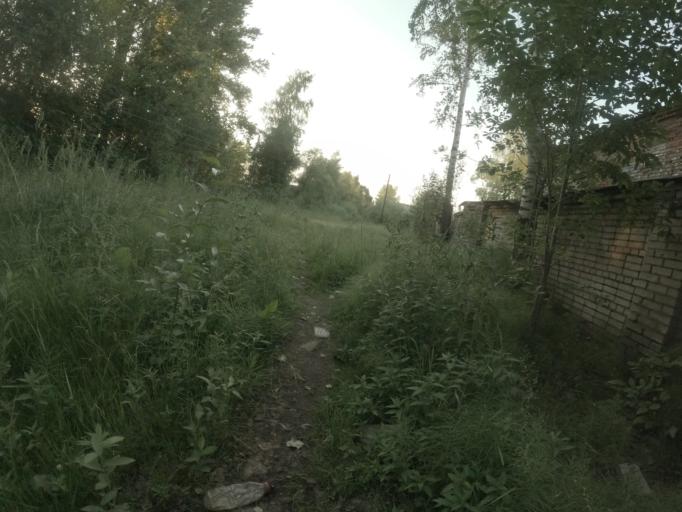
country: RU
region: St.-Petersburg
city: Krasnogvargeisky
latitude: 59.9440
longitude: 30.4405
